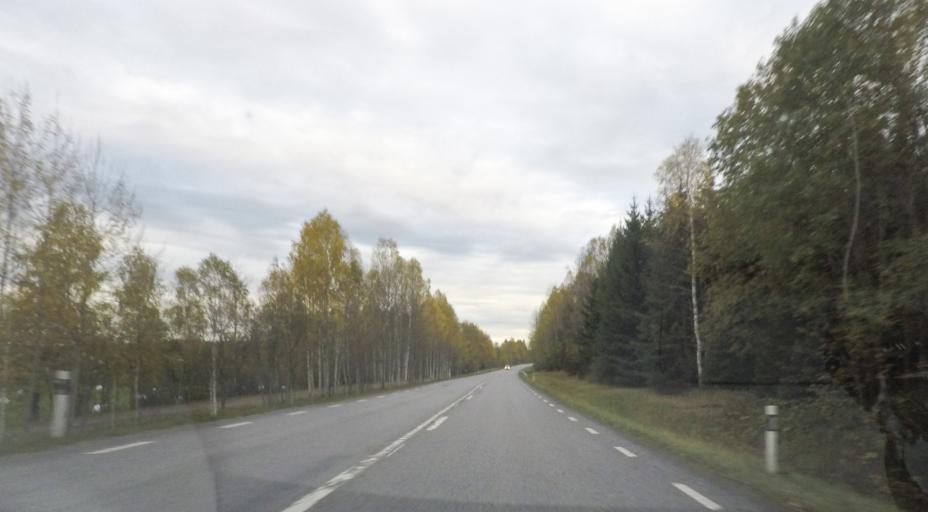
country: SE
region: OErebro
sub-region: Nora Kommun
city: As
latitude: 59.5095
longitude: 14.9887
